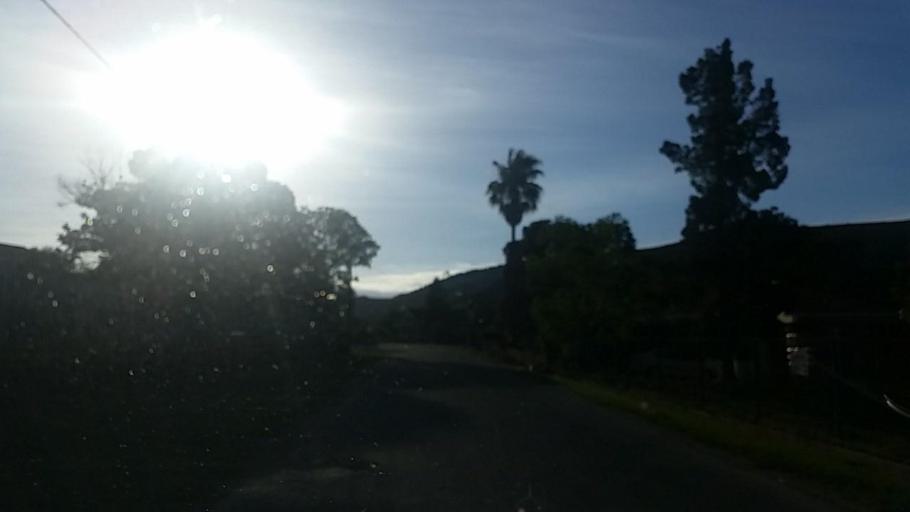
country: ZA
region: Western Cape
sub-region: Eden District Municipality
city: Knysna
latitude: -33.6537
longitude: 23.1307
